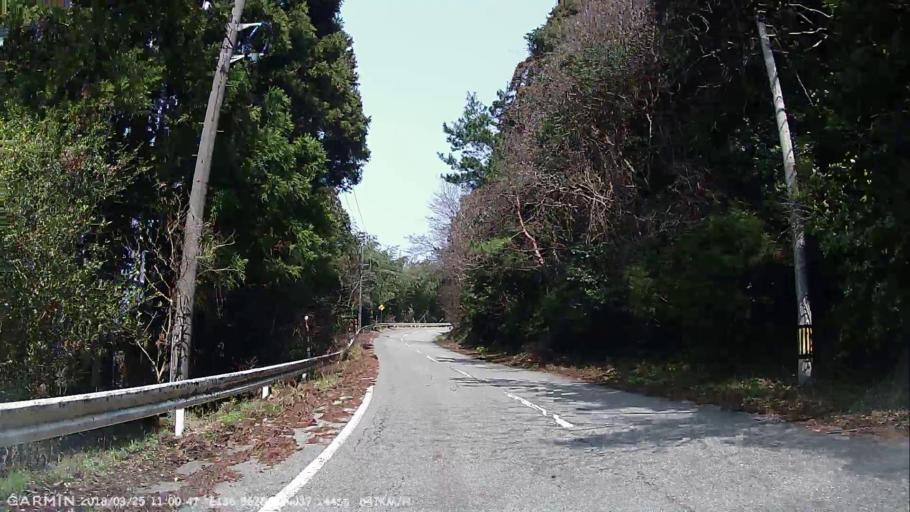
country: JP
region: Ishikawa
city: Nanao
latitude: 37.1447
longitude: 136.9639
